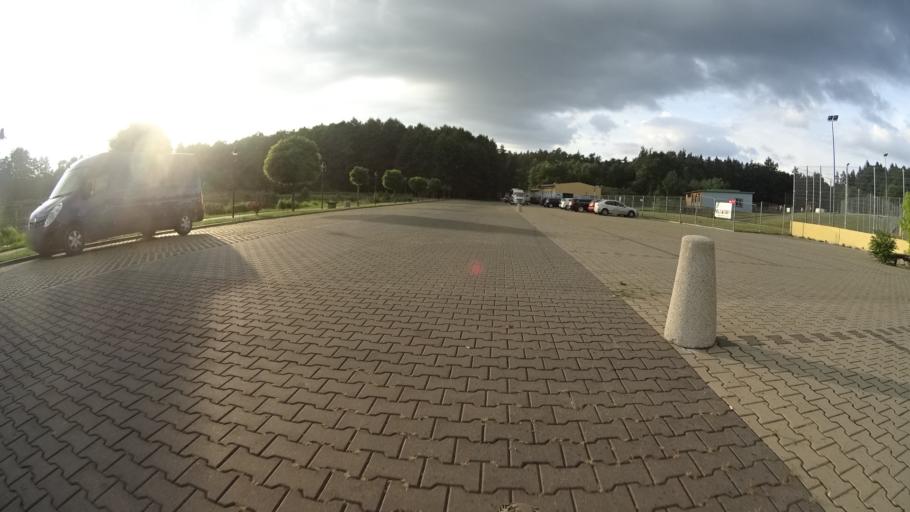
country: PL
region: Masovian Voivodeship
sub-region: Powiat grojecki
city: Mogielnica
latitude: 51.6980
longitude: 20.7246
